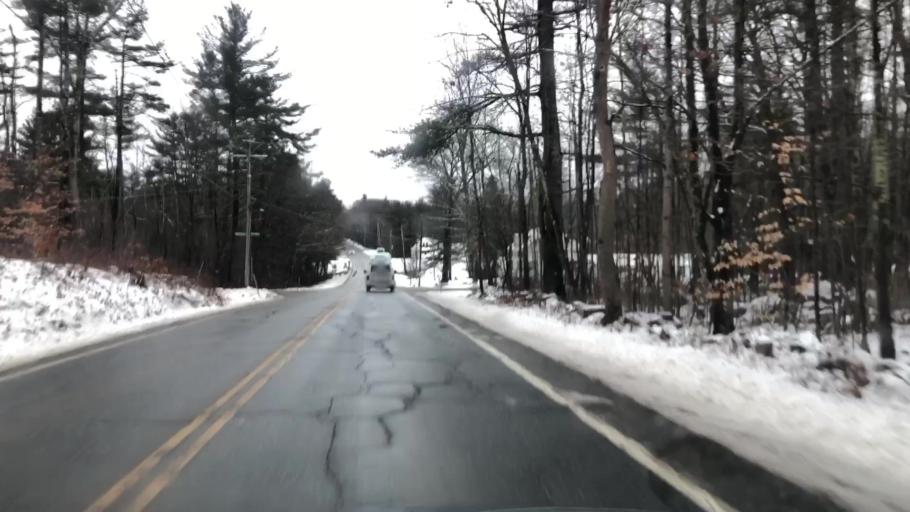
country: US
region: New Hampshire
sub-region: Hillsborough County
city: New Boston
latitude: 43.0180
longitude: -71.6896
